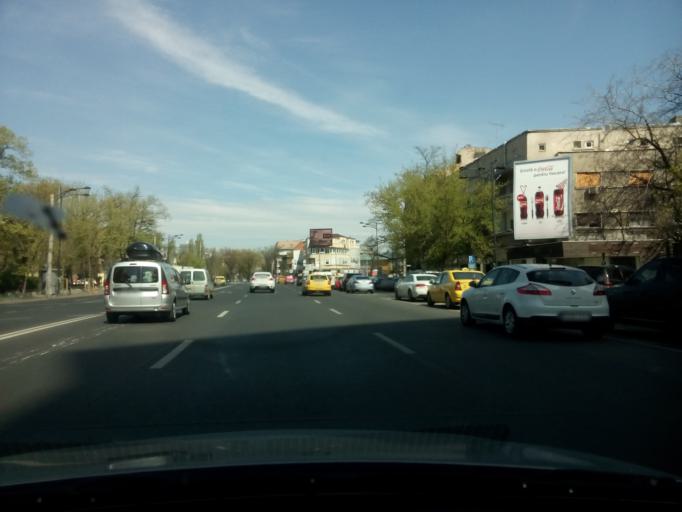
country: RO
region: Bucuresti
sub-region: Municipiul Bucuresti
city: Bucharest
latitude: 44.4593
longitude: 26.0950
